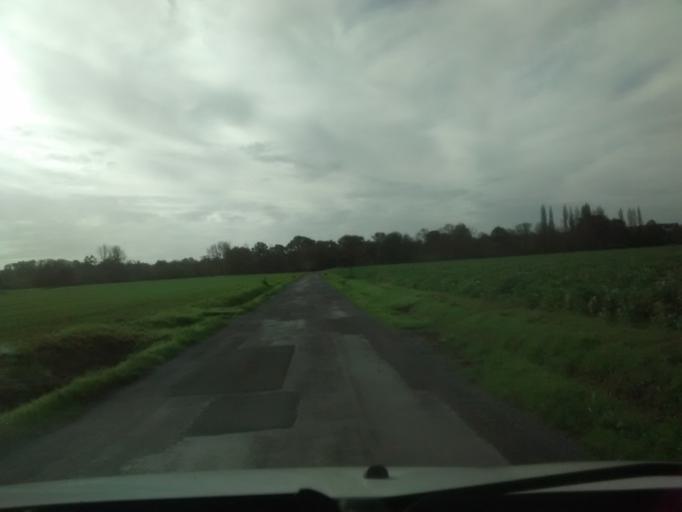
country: FR
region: Brittany
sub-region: Departement d'Ille-et-Vilaine
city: Brece
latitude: 48.1178
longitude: -1.4812
